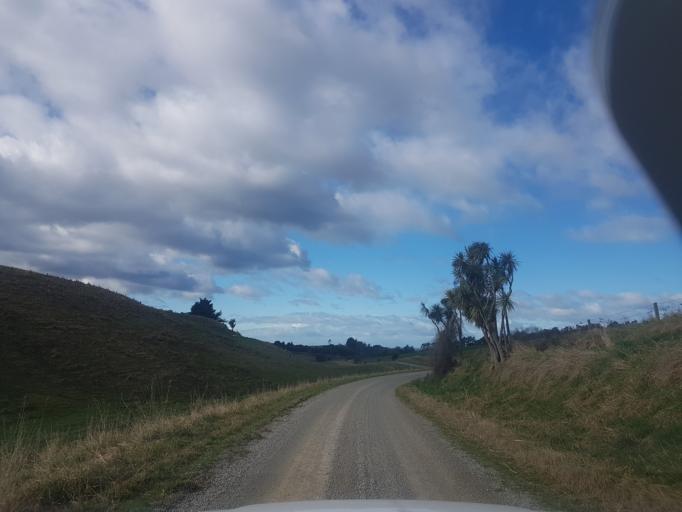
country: NZ
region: Canterbury
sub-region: Timaru District
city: Pleasant Point
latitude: -44.1835
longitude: 171.1328
